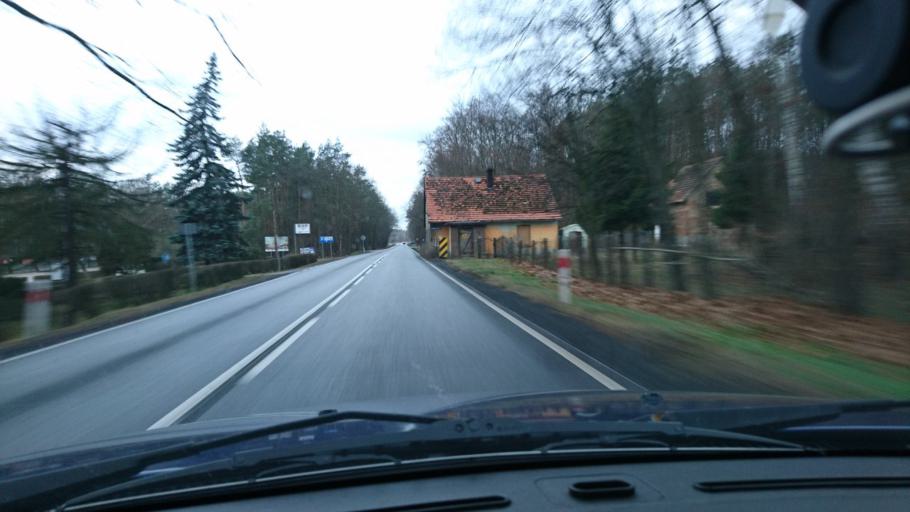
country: PL
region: Opole Voivodeship
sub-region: Powiat kluczborski
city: Kluczbork
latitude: 50.9648
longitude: 18.2791
